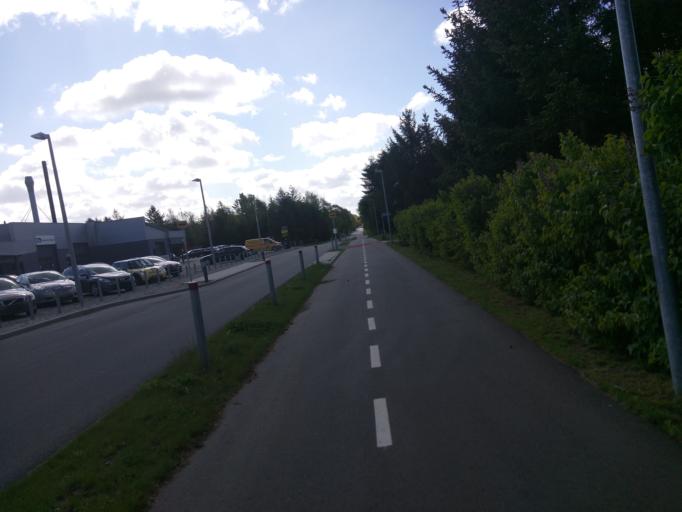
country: DK
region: Central Jutland
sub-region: Viborg Kommune
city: Viborg
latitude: 56.4172
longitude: 9.4092
